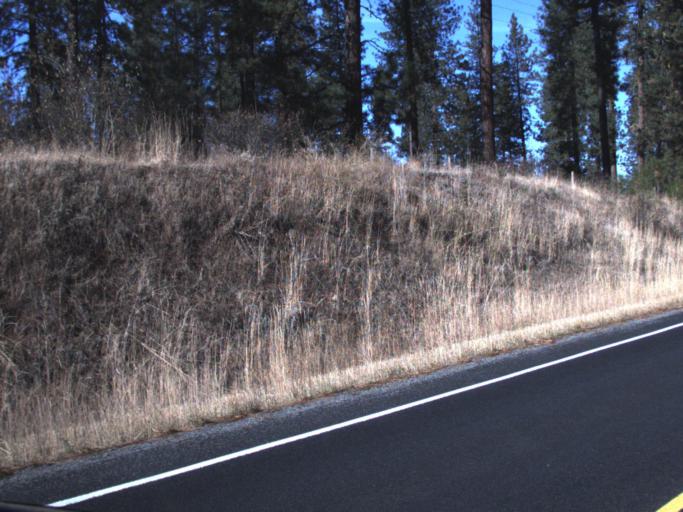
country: US
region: Washington
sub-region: Lincoln County
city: Davenport
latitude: 47.9527
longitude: -118.3122
